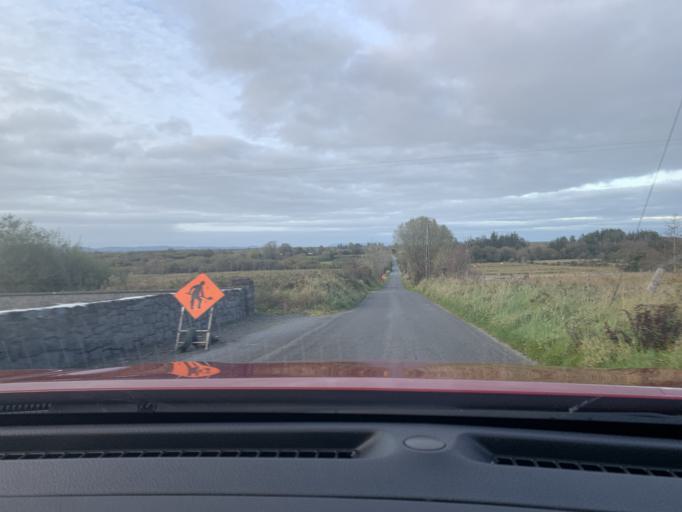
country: IE
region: Connaught
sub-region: Roscommon
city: Ballaghaderreen
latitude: 53.9787
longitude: -8.6178
